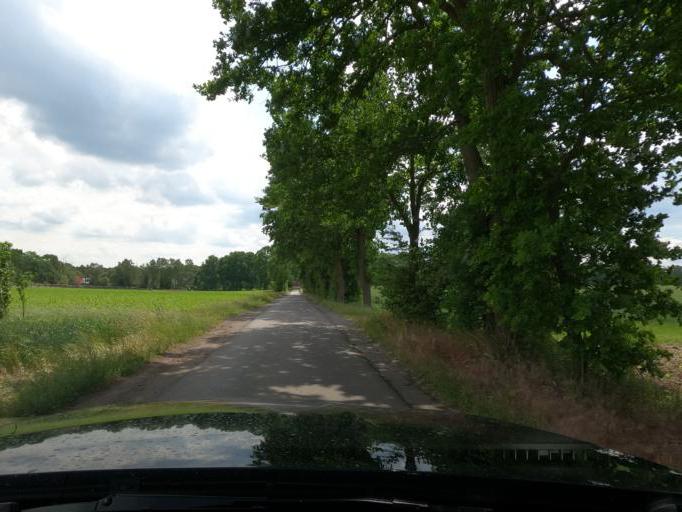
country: DE
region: Lower Saxony
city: Steimbke
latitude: 52.6322
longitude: 9.4251
